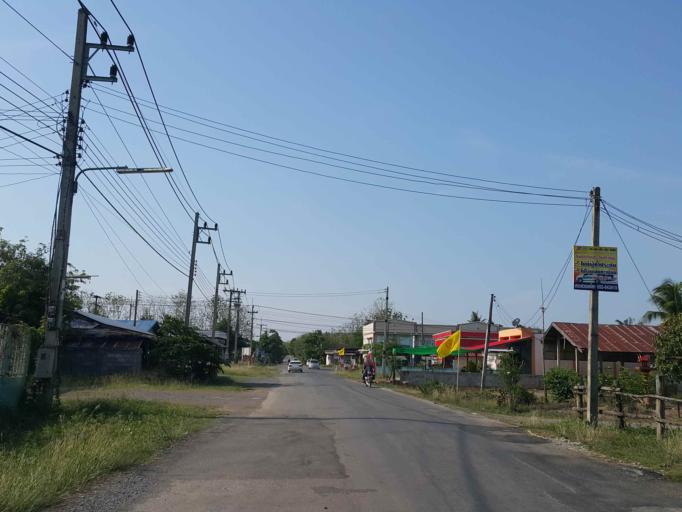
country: TH
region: Sukhothai
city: Thung Saliam
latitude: 17.3325
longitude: 99.5501
